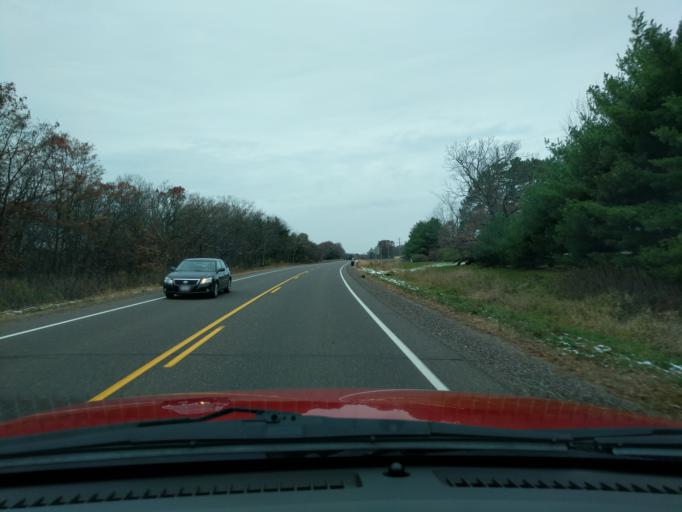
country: US
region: Wisconsin
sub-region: Burnett County
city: Siren
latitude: 45.8246
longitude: -92.2580
